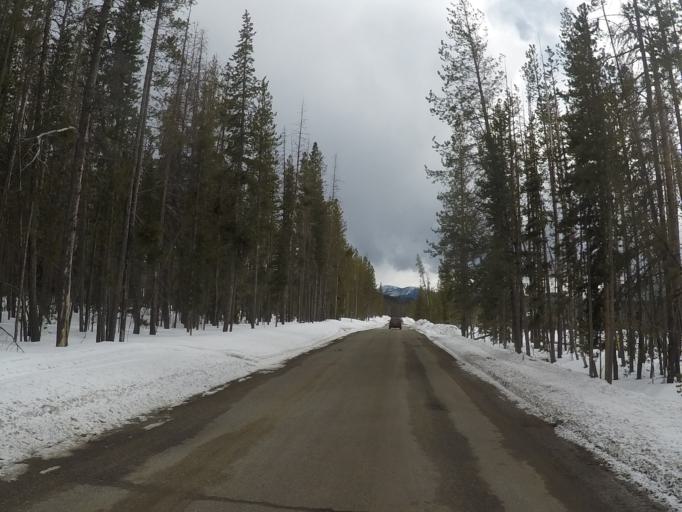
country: US
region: Montana
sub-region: Granite County
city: Philipsburg
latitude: 46.2068
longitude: -113.2509
